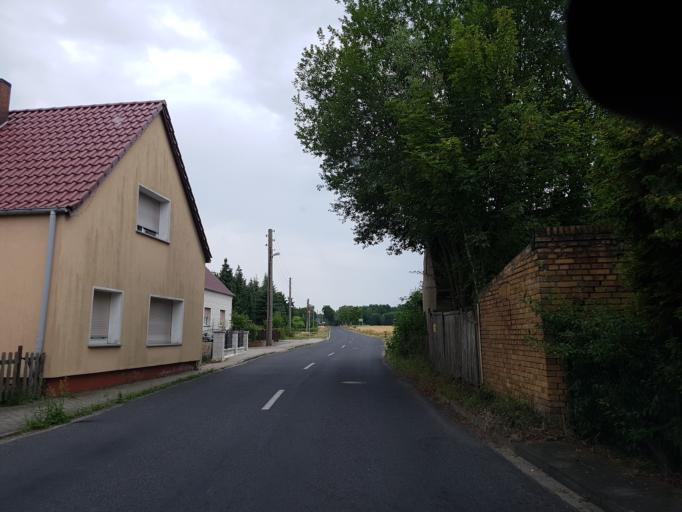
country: DE
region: Brandenburg
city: Sallgast
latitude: 51.5863
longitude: 13.8487
